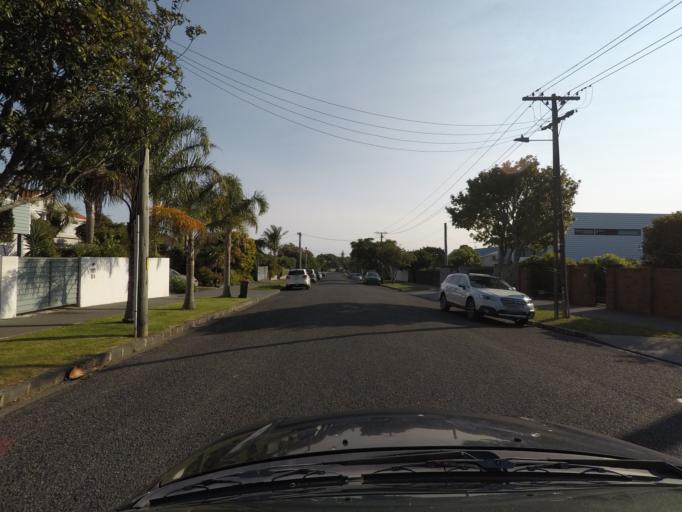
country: NZ
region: Auckland
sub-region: Auckland
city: Rosebank
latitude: -36.8584
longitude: 174.7012
